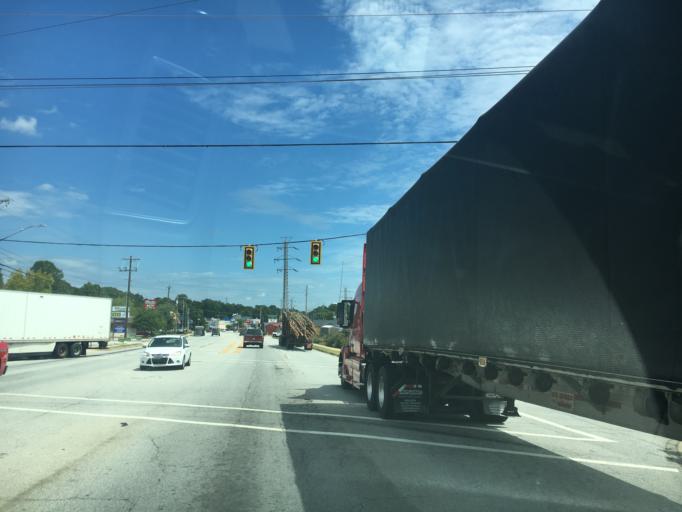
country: US
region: South Carolina
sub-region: Laurens County
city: Laurens
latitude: 34.5051
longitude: -82.0164
